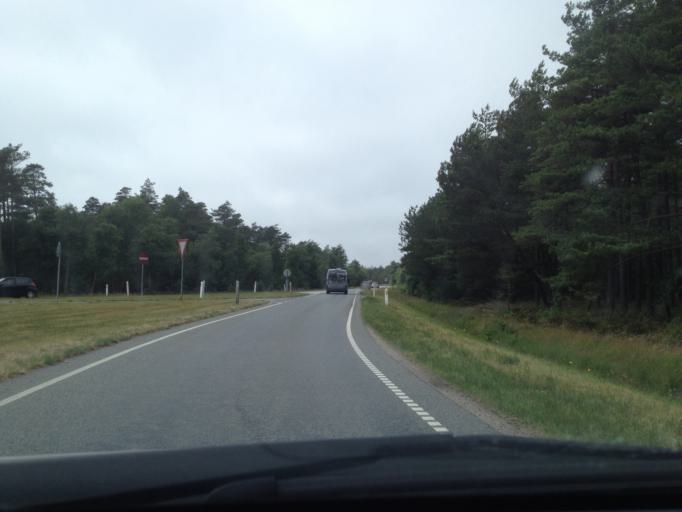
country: DK
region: South Denmark
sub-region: Varde Kommune
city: Oksbol
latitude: 55.5786
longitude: 8.2284
